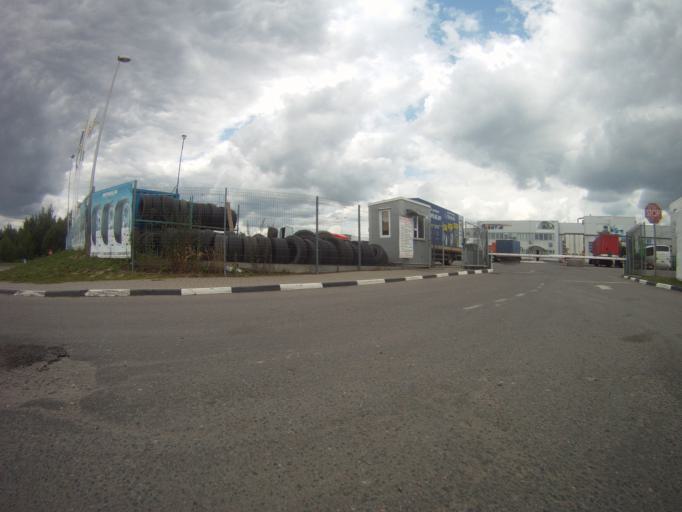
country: BY
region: Minsk
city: Malinovka
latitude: 53.8784
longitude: 27.4108
